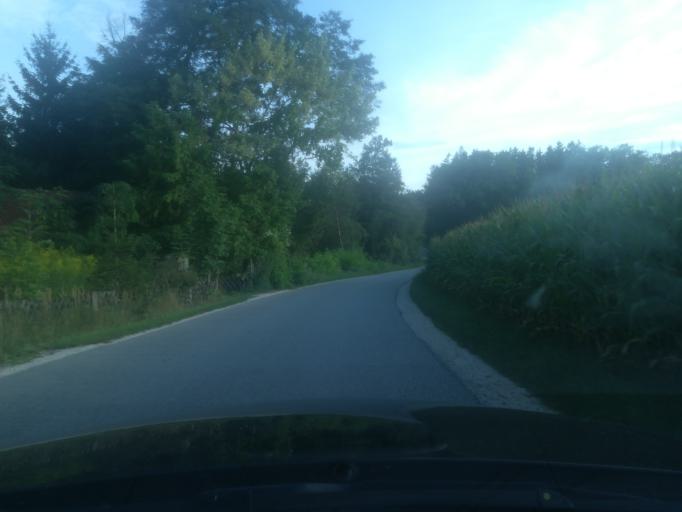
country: AT
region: Upper Austria
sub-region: Wels-Land
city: Marchtrenk
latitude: 48.1592
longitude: 14.1685
